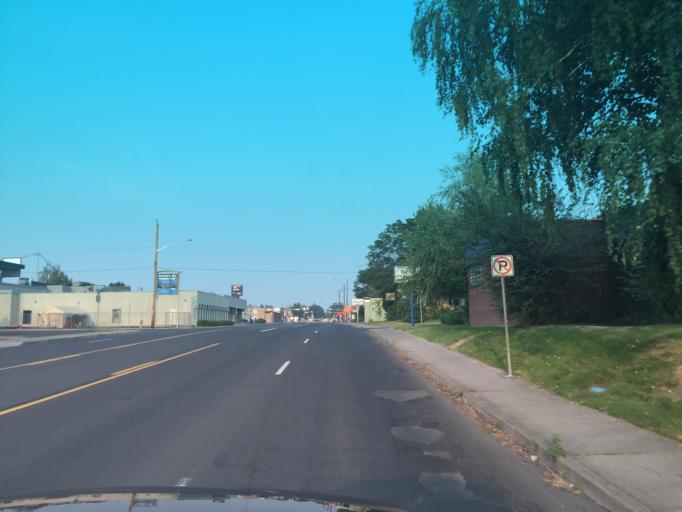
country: US
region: Washington
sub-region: Spokane County
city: Spokane
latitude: 47.6749
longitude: -117.4152
